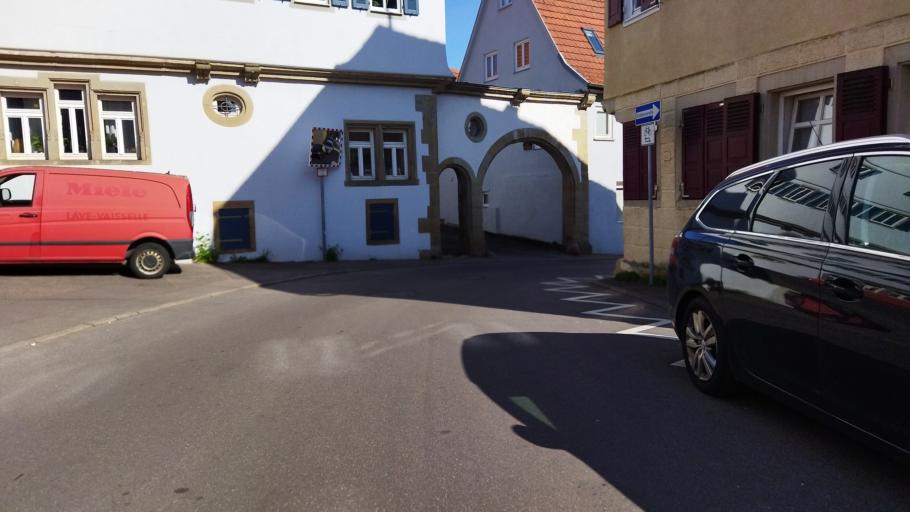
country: DE
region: Baden-Wuerttemberg
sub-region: Regierungsbezirk Stuttgart
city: Bietigheim-Bissingen
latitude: 48.9613
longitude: 9.1028
